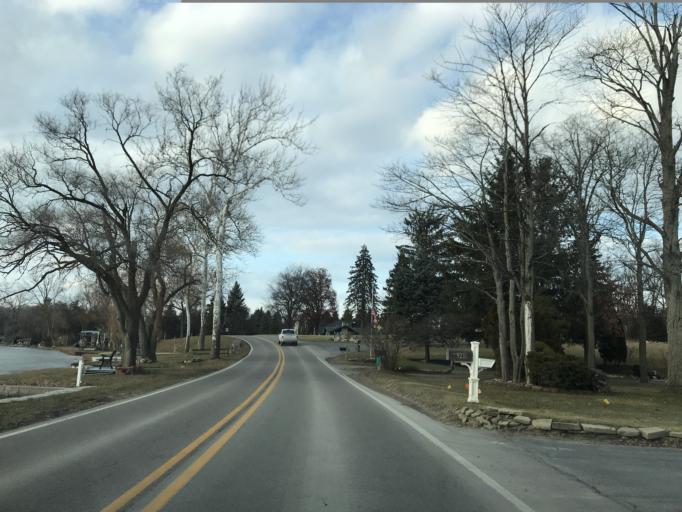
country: US
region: Michigan
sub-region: Livingston County
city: Whitmore Lake
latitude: 42.4680
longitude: -83.7172
